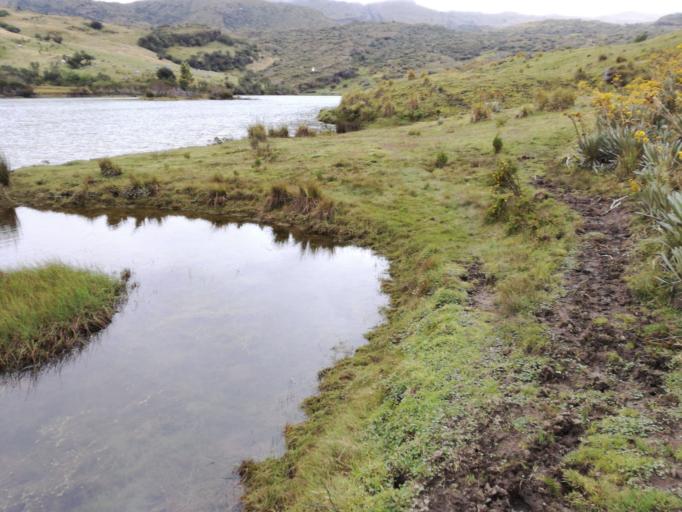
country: CO
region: Boyaca
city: Socha Viejo
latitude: 5.8924
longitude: -72.6765
